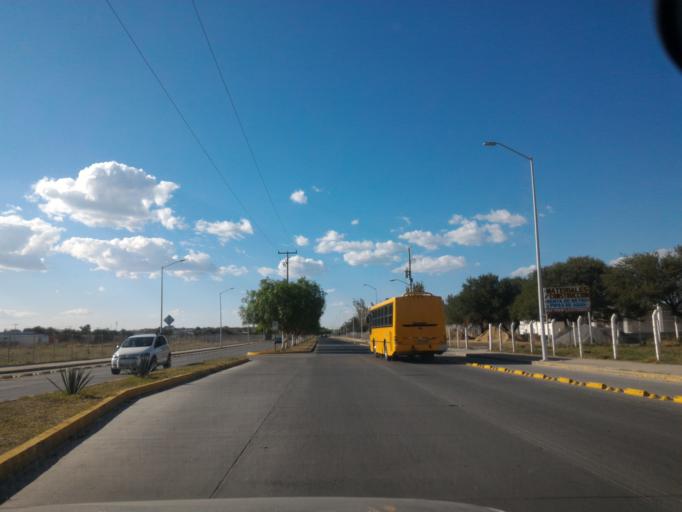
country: MX
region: Guanajuato
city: San Francisco del Rincon
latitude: 21.0313
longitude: -101.8695
